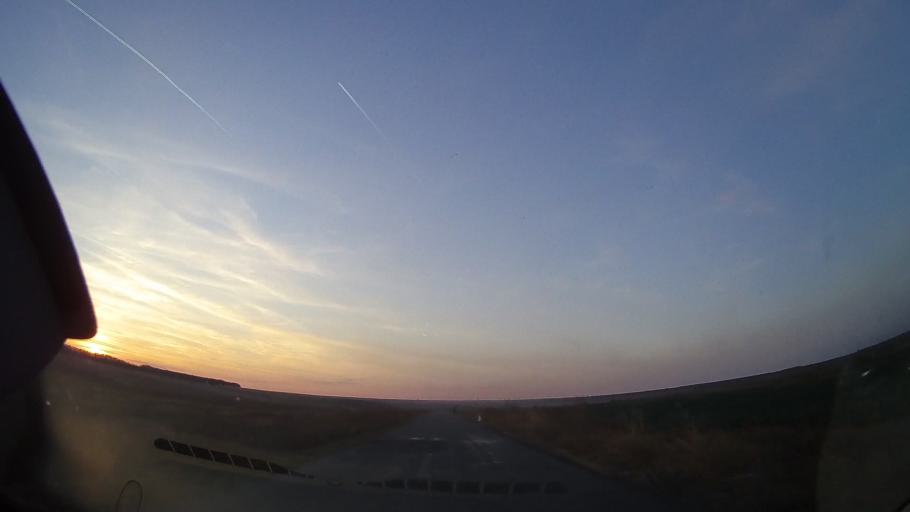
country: RO
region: Constanta
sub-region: Comuna Mereni
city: Mereni
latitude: 44.0166
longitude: 28.3065
